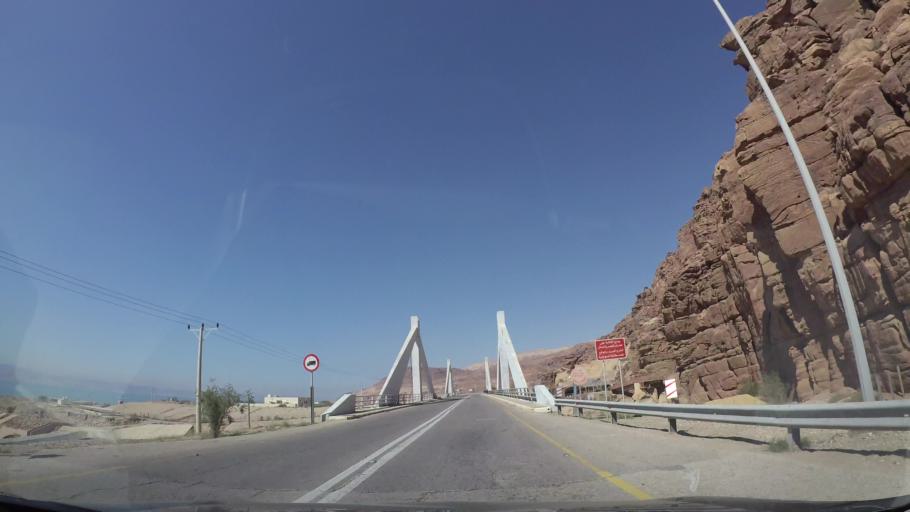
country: JO
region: Karak
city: Al Qasr
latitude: 31.4657
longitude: 35.5726
